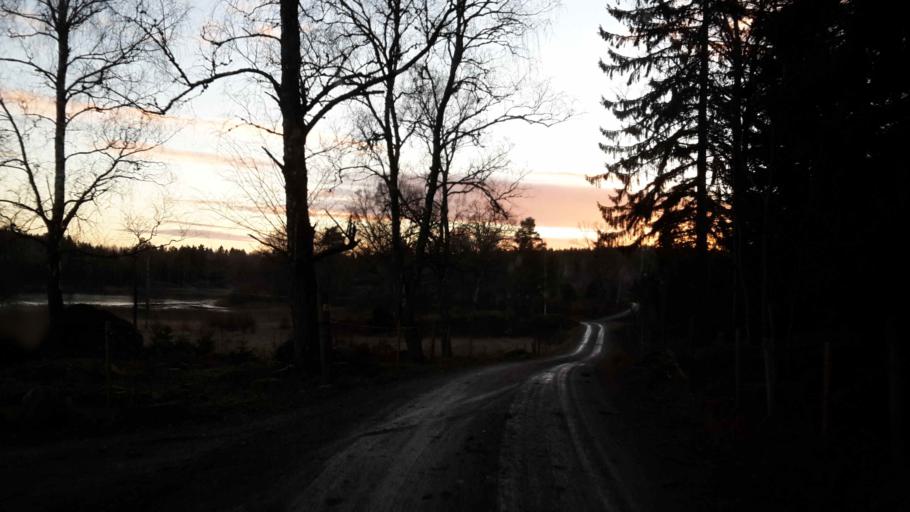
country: SE
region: OEstergoetland
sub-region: Atvidabergs Kommun
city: Atvidaberg
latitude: 58.2723
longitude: 16.0779
